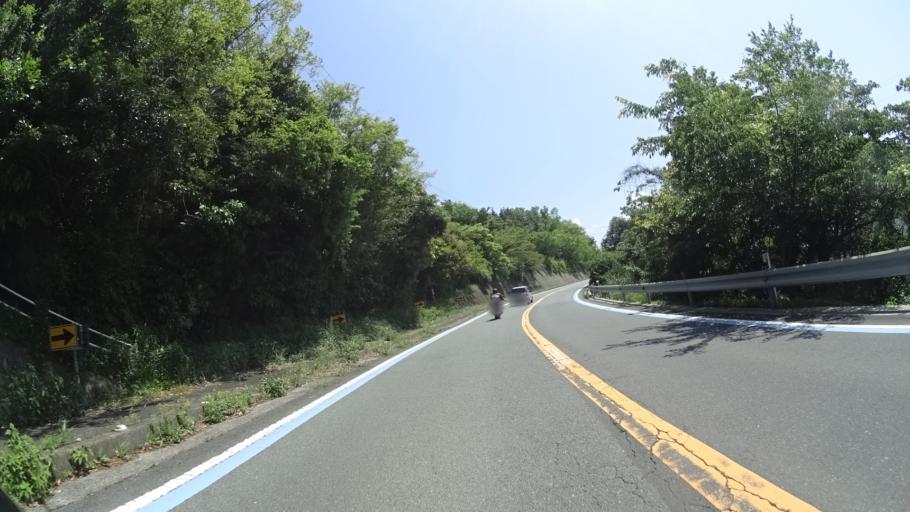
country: JP
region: Ehime
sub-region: Nishiuwa-gun
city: Ikata-cho
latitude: 33.4795
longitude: 132.3016
